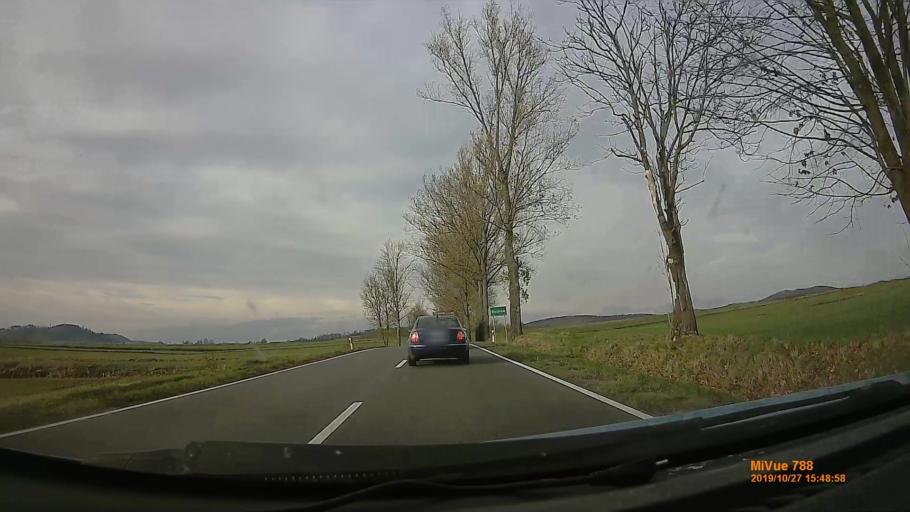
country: PL
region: Lower Silesian Voivodeship
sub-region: Powiat klodzki
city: Bozkow
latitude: 50.5026
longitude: 16.5846
